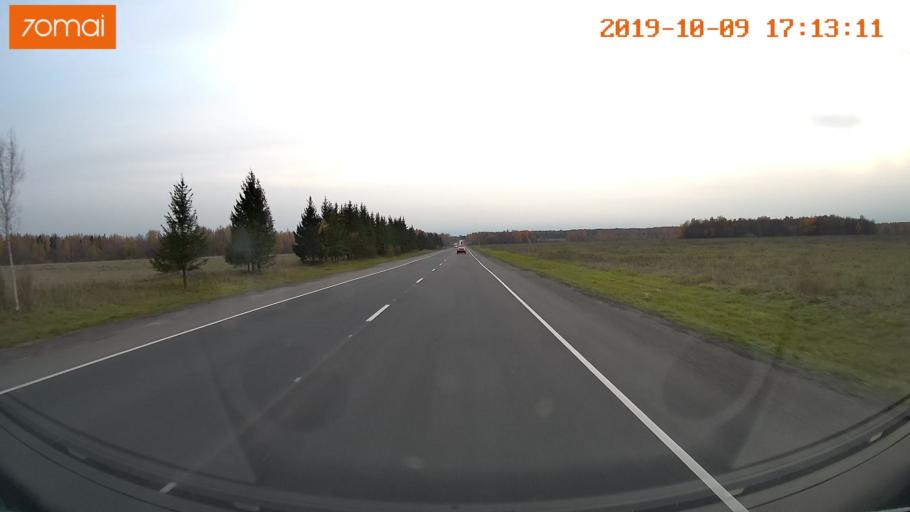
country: RU
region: Ivanovo
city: Privolzhsk
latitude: 57.3182
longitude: 41.2281
